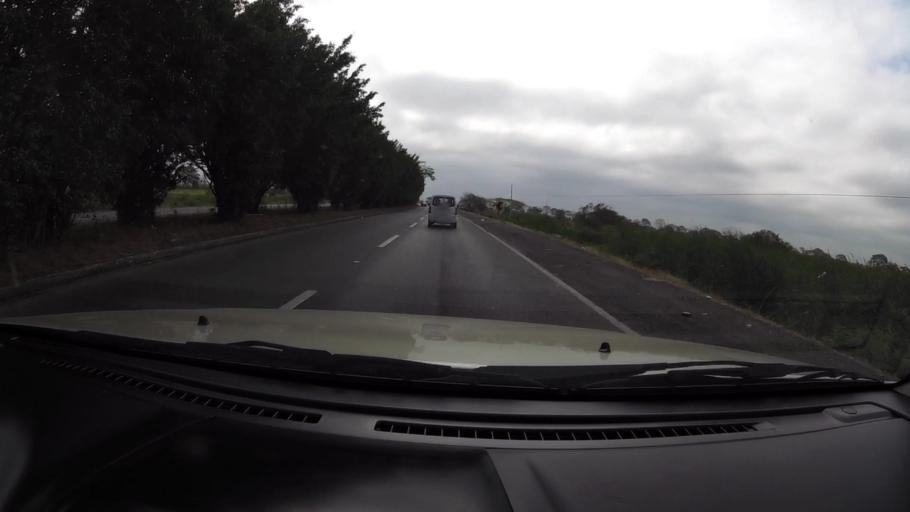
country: EC
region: Guayas
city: Eloy Alfaro
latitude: -2.2075
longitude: -79.7417
